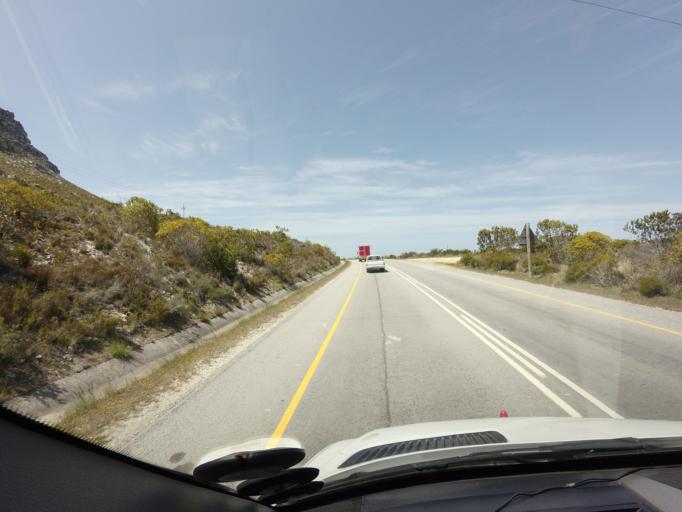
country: ZA
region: Western Cape
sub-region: Overberg District Municipality
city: Grabouw
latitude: -34.3329
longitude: 18.9929
